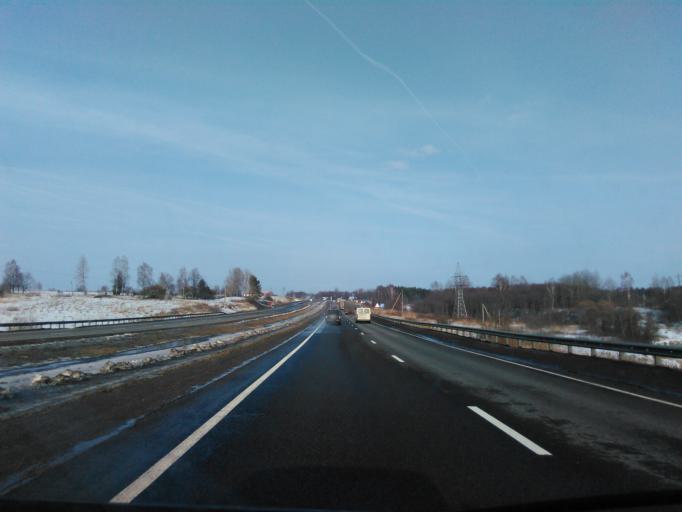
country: RU
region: Smolensk
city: Vyaz'ma
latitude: 55.2066
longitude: 34.1510
